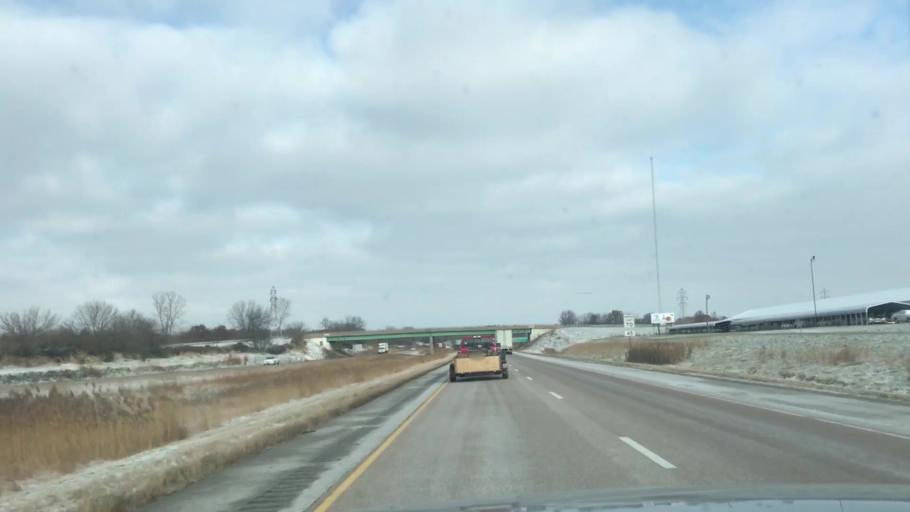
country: US
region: Illinois
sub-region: Macoupin County
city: Staunton
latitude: 39.0299
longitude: -89.7521
